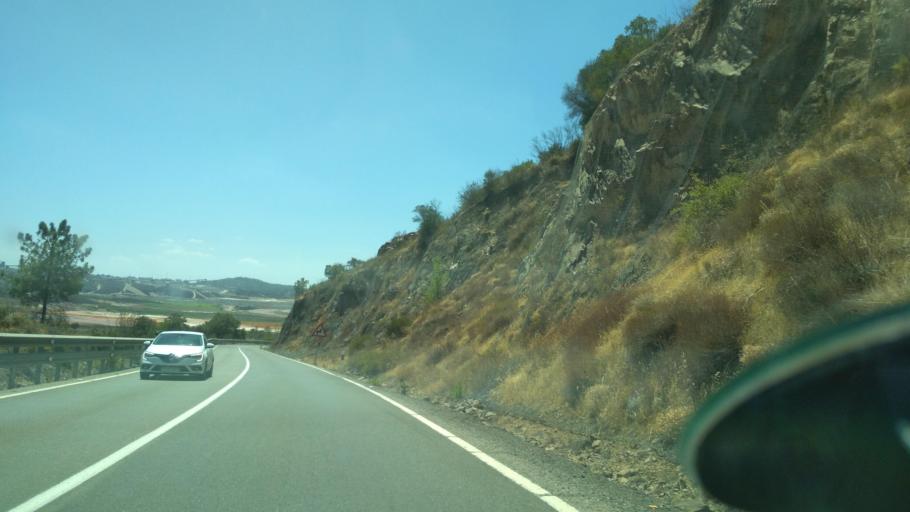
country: ES
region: Andalusia
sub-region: Provincia de Huelva
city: Campofrio
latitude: 37.7434
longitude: -6.5855
